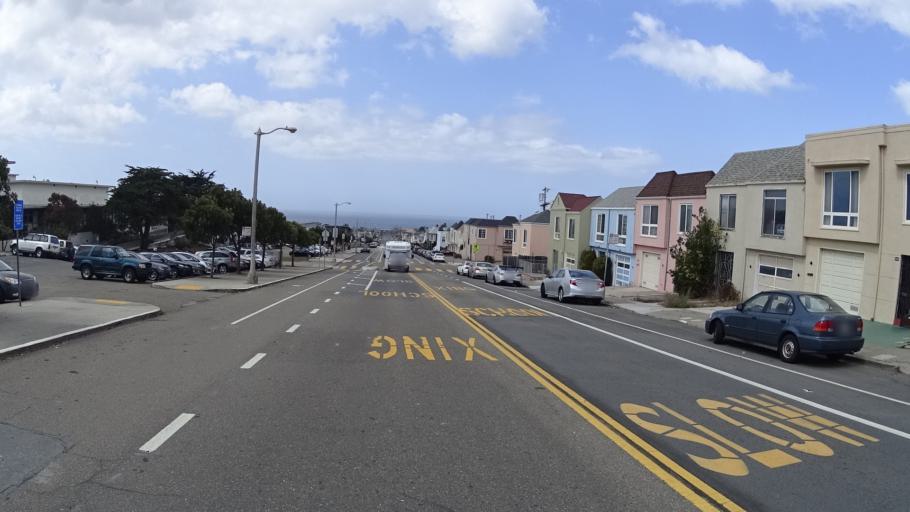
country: US
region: California
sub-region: San Mateo County
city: Daly City
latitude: 37.7515
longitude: -122.4959
